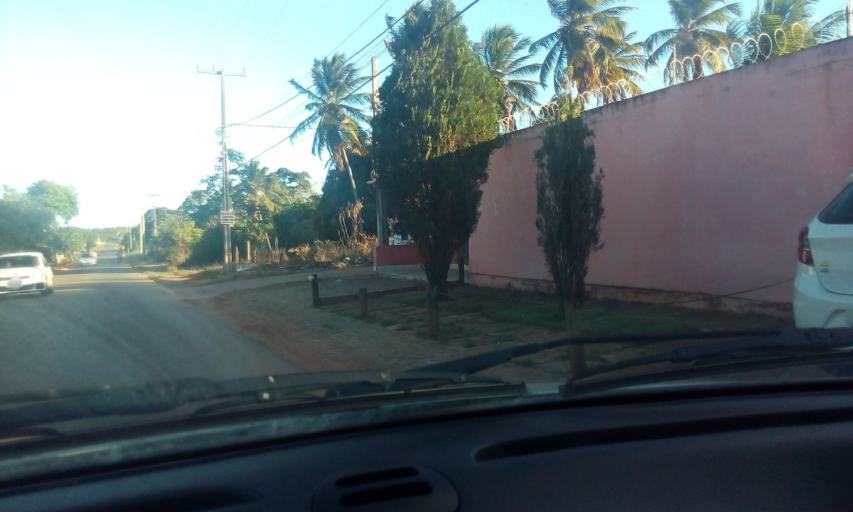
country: BR
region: Rio Grande do Norte
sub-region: Parnamirim
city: Parnamirim
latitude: -5.9520
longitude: -35.1761
